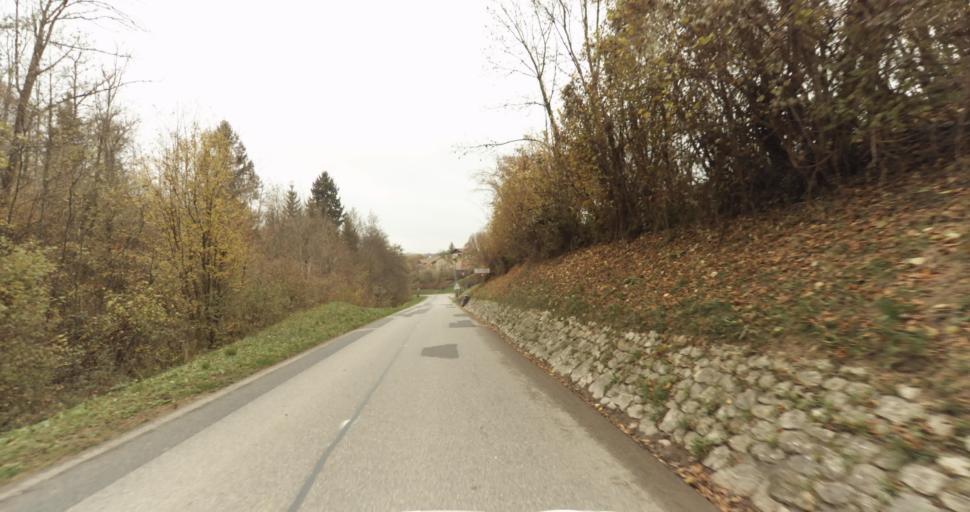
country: FR
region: Rhone-Alpes
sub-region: Departement de la Haute-Savoie
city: Alby-sur-Cheran
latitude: 45.8124
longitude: 6.0287
